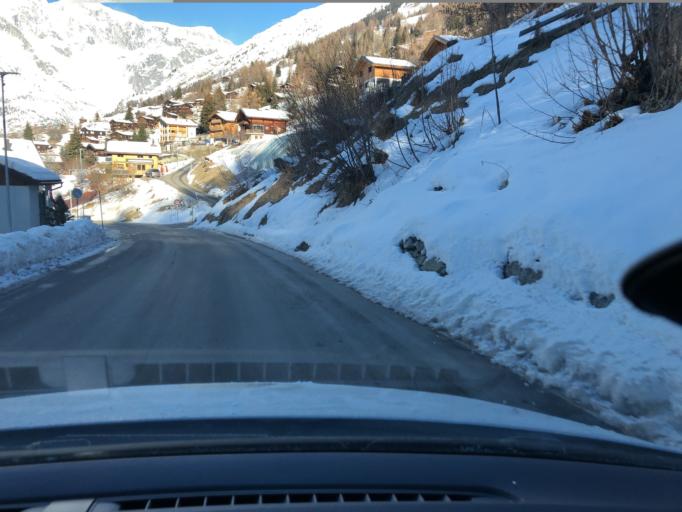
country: CH
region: Valais
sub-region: Goms District
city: Fiesch
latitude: 46.4276
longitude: 8.1581
